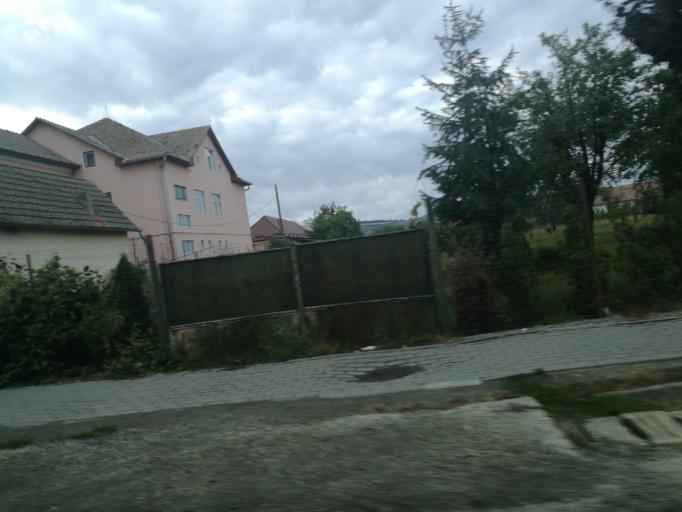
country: RO
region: Mures
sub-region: Comuna Ungheni
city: Ungheni
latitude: 46.4848
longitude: 24.4586
